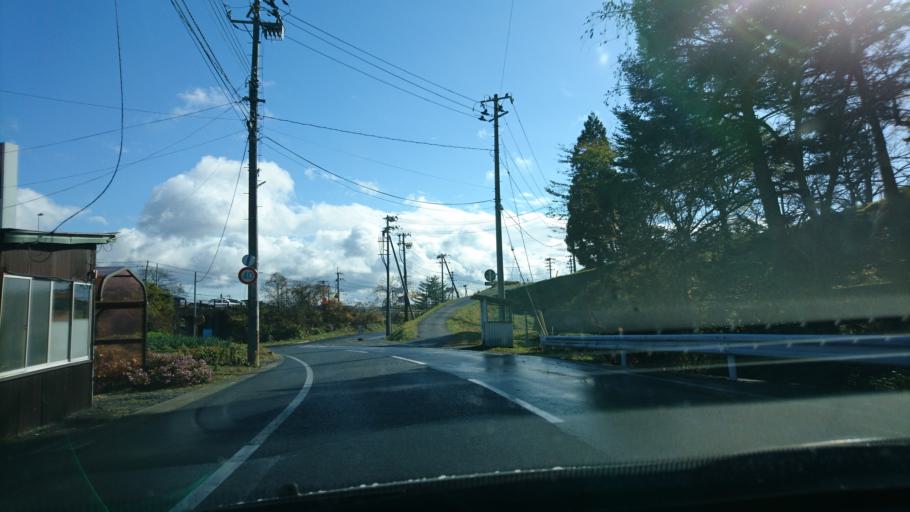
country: JP
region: Iwate
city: Ichinoseki
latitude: 38.9394
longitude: 141.1181
